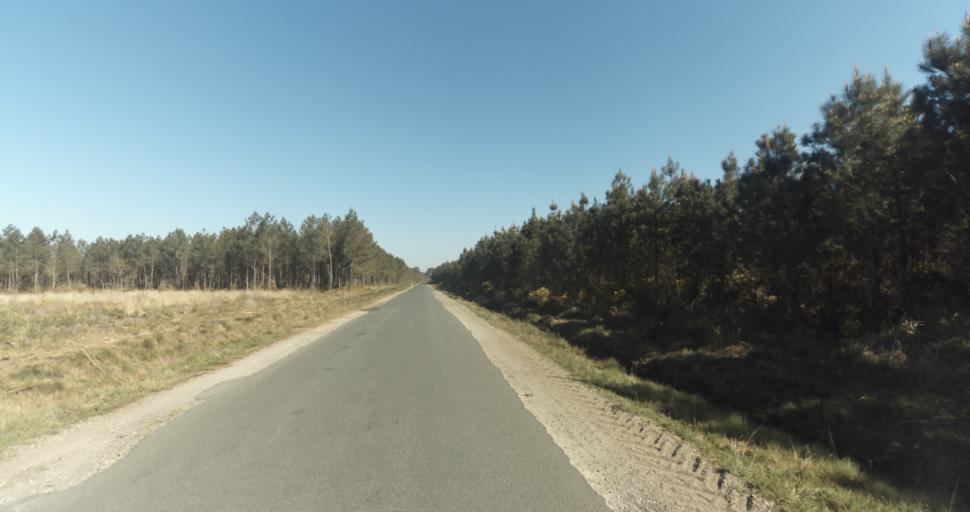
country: FR
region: Aquitaine
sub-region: Departement de la Gironde
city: Marcheprime
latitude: 44.7518
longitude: -0.8484
